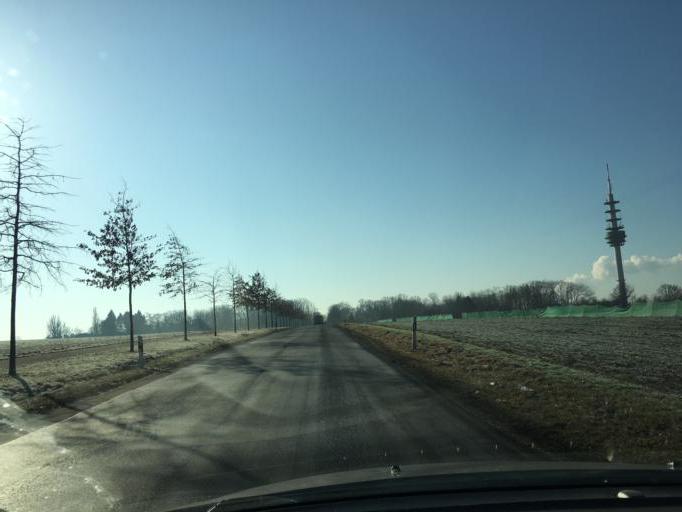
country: DE
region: Saxony
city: Taucha
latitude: 51.3214
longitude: 12.4519
